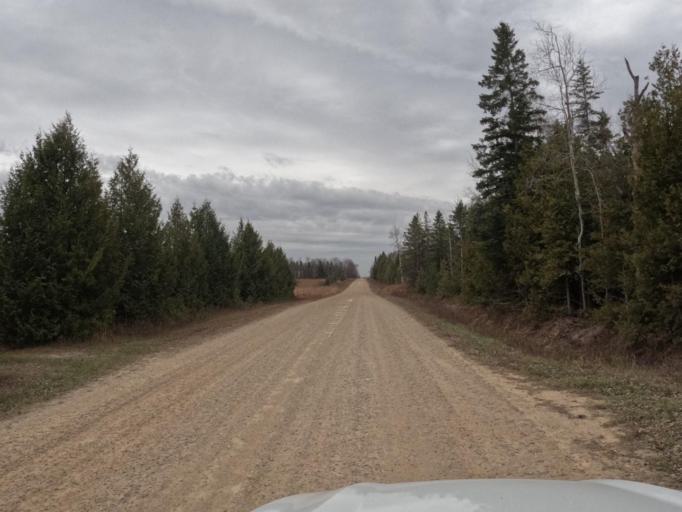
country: CA
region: Ontario
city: Shelburne
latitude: 44.0275
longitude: -80.3934
